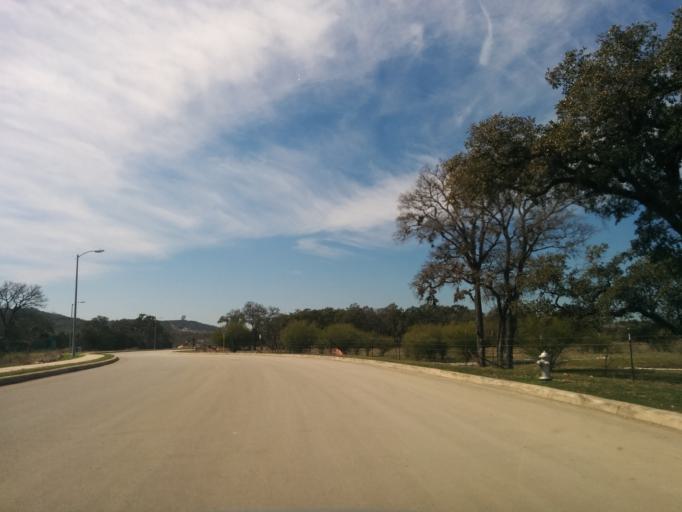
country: US
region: Texas
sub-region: Bexar County
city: Cross Mountain
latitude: 29.6684
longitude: -98.6333
